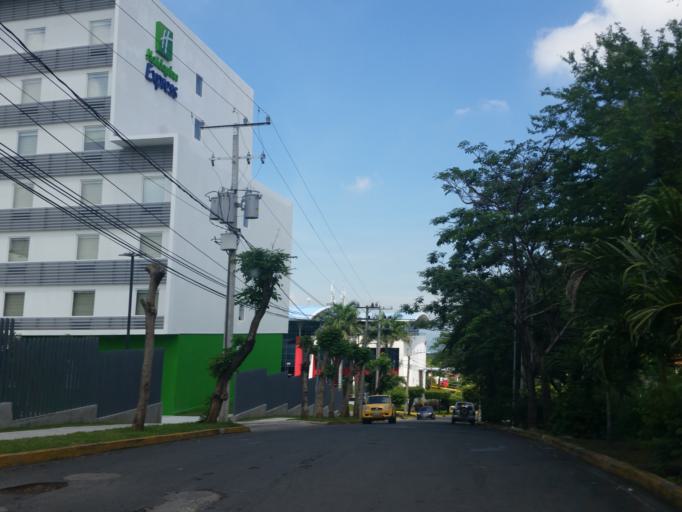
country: NI
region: Managua
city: Managua
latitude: 12.1033
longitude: -86.2556
